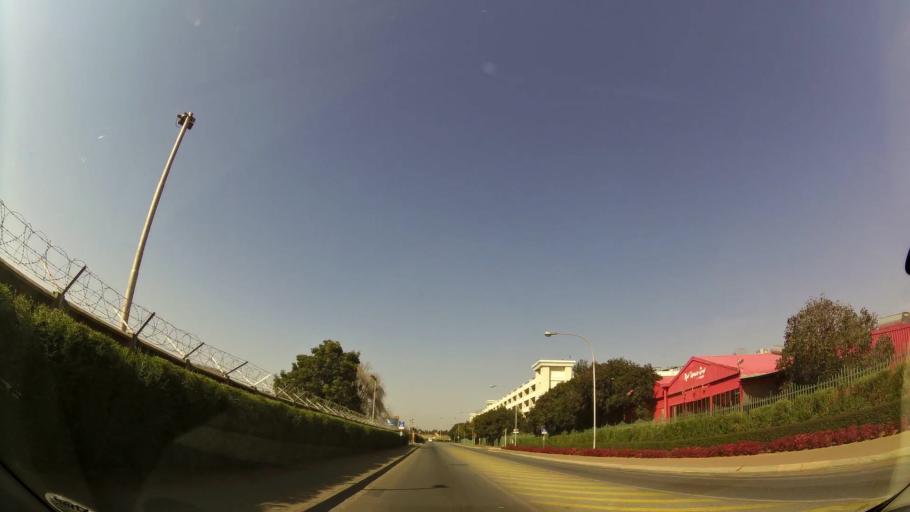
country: ZA
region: Gauteng
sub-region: Ekurhuleni Metropolitan Municipality
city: Boksburg
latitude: -26.1430
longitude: 28.2233
